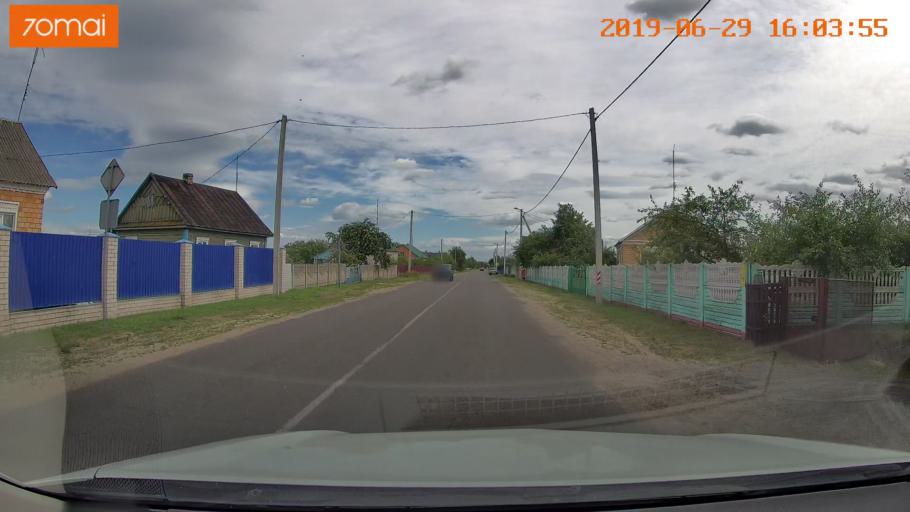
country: BY
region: Brest
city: Luninyets
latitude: 52.2268
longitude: 27.0219
